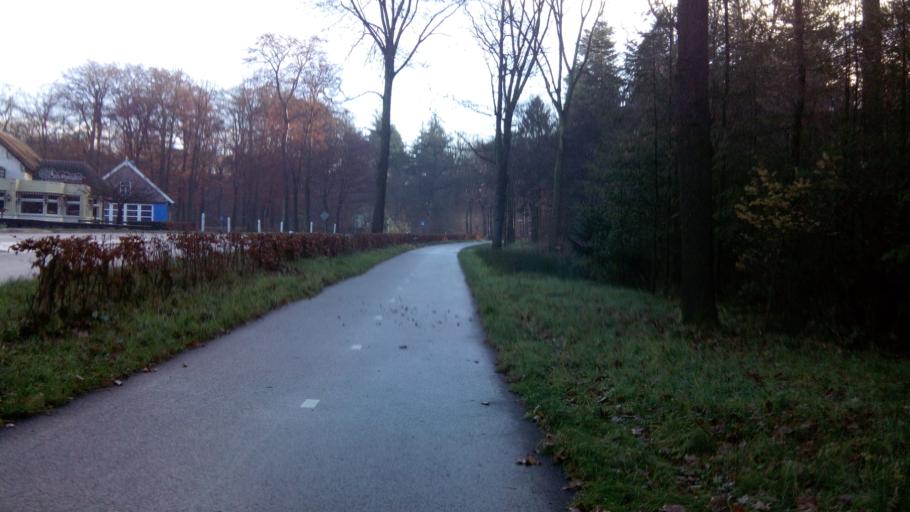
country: NL
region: Utrecht
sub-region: Gemeente Utrechtse Heuvelrug
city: Maarn
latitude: 52.0870
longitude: 5.3370
